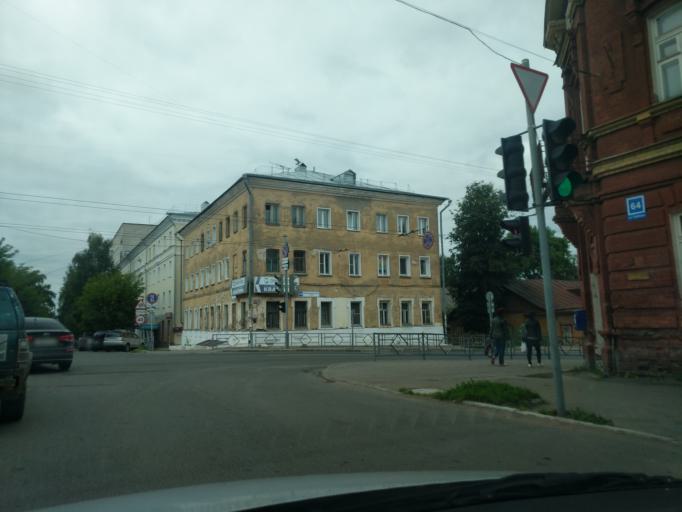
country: RU
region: Kirov
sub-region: Kirovo-Chepetskiy Rayon
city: Kirov
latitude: 58.6052
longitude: 49.6767
